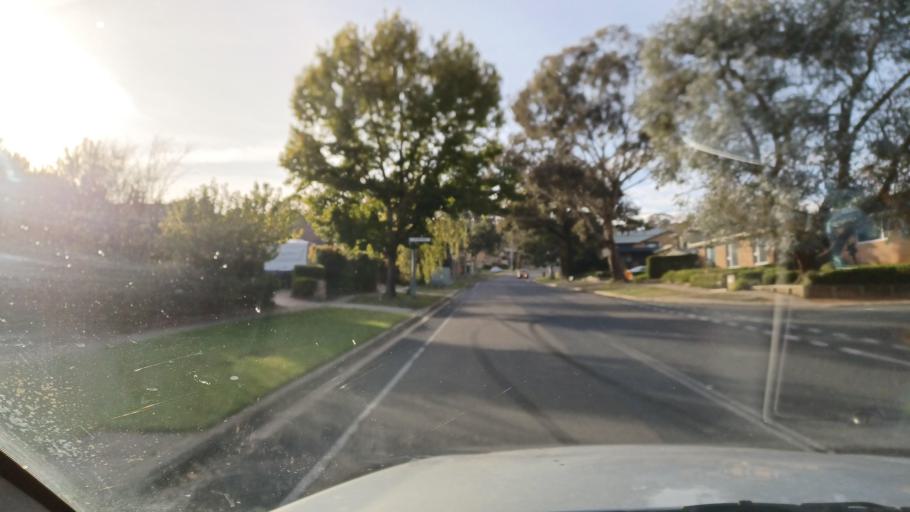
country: AU
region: Australian Capital Territory
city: Belconnen
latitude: -35.1993
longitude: 149.0460
